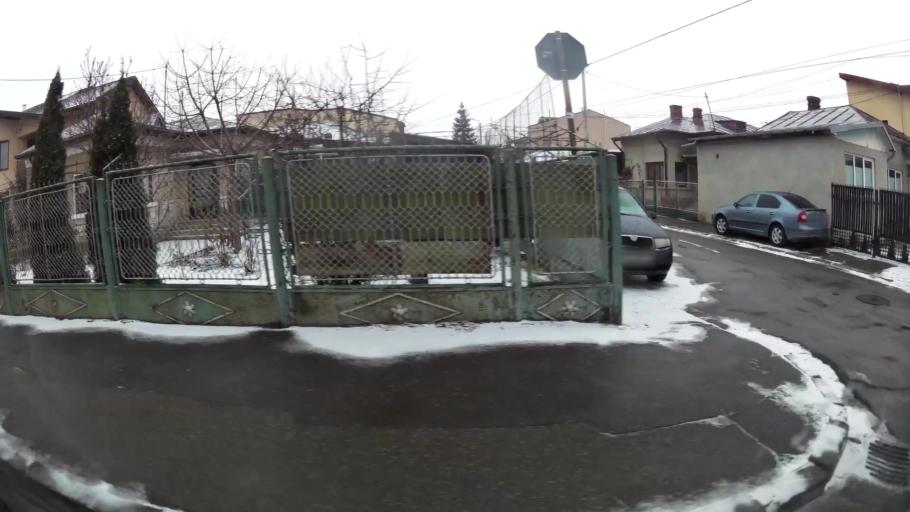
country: RO
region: Prahova
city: Ploiesti
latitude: 44.9494
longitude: 26.0218
